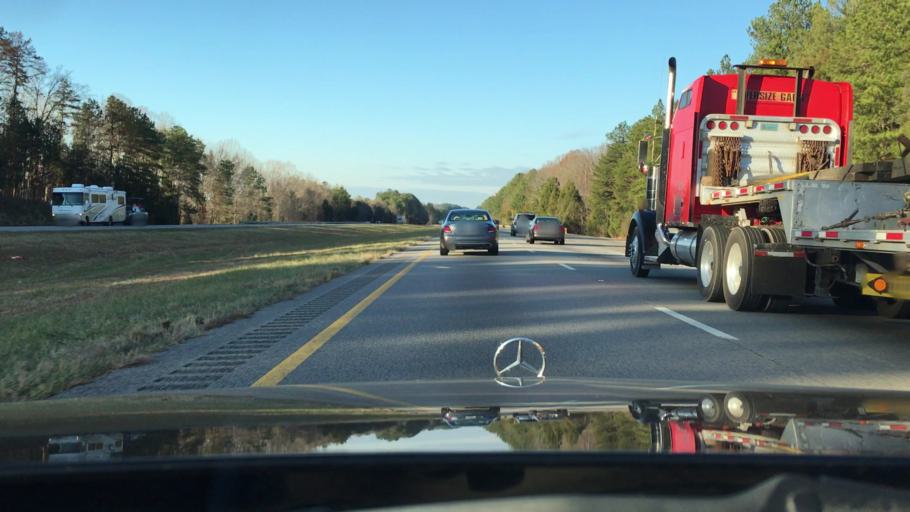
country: US
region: South Carolina
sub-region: Chester County
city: Eureka Mill
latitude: 34.7167
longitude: -81.0317
